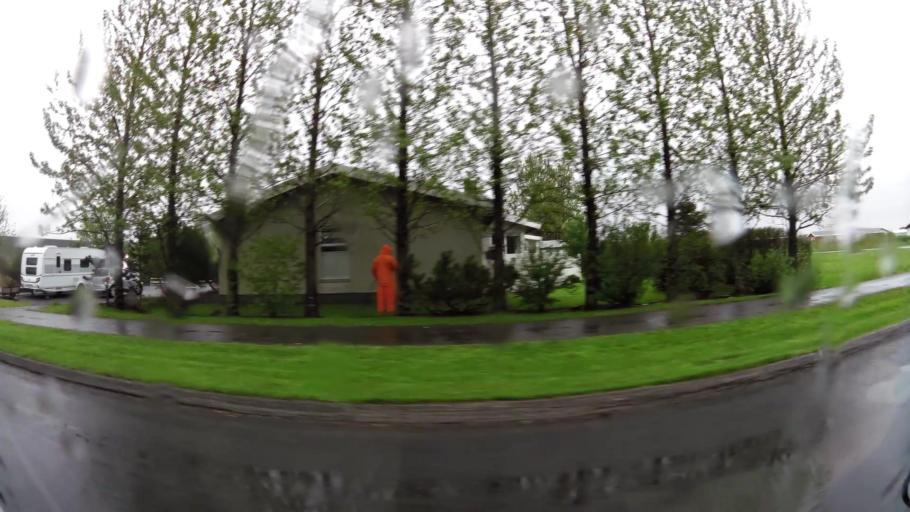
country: IS
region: South
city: Selfoss
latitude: 63.9265
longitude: -20.9917
